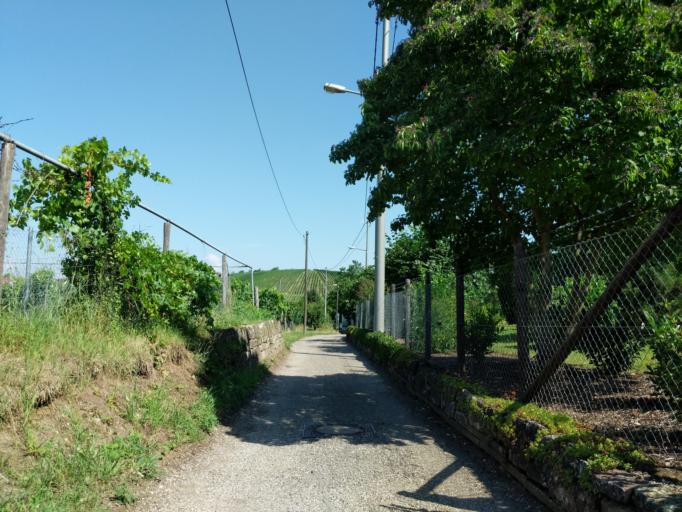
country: DE
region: Baden-Wuerttemberg
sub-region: Regierungsbezirk Stuttgart
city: Fellbach
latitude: 48.7868
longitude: 9.2660
